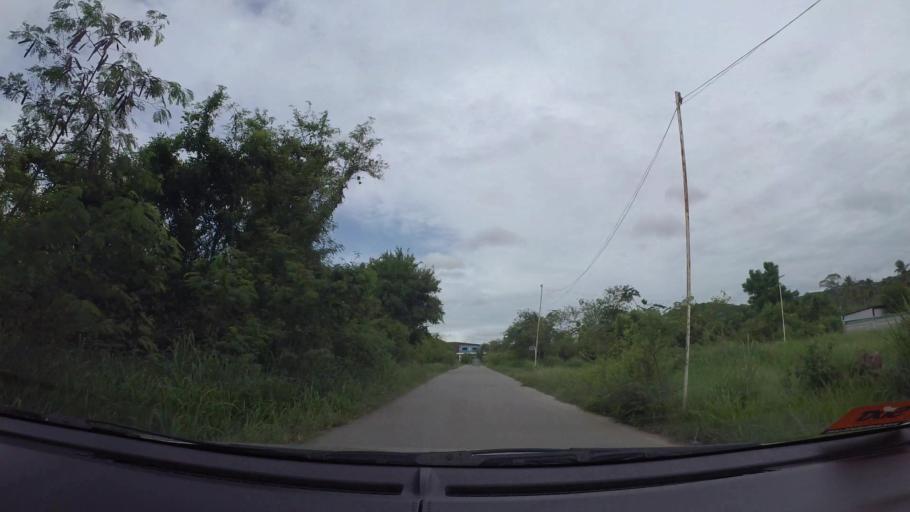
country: TH
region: Chon Buri
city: Sattahip
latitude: 12.7156
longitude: 100.9050
